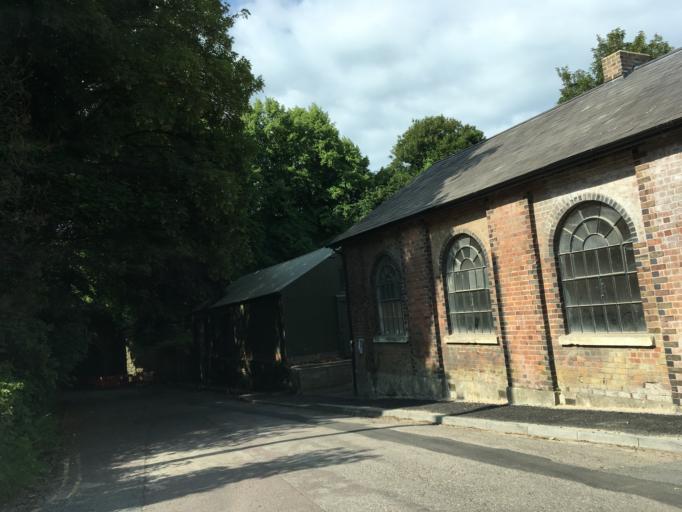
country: GB
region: England
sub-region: Gloucestershire
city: Brimscombe
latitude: 51.7185
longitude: -2.1813
